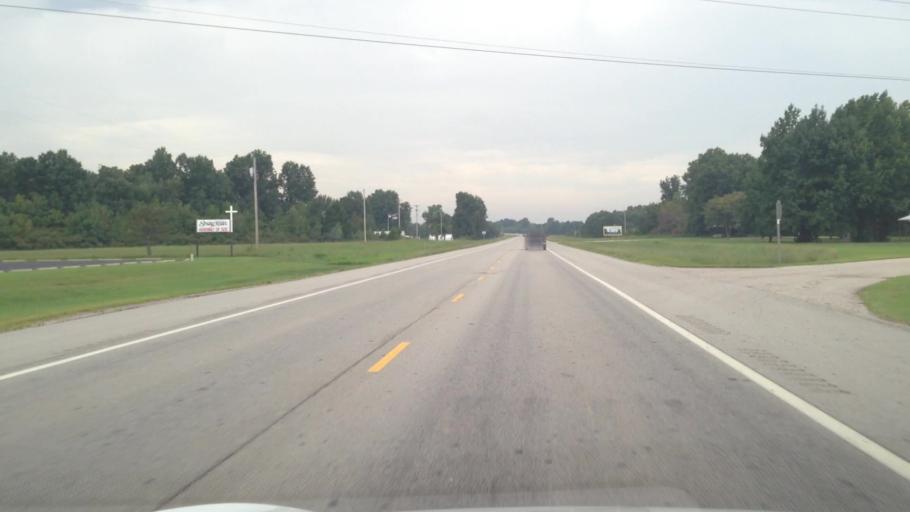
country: US
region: Kansas
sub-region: Cherokee County
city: Baxter Springs
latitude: 37.0678
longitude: -94.7246
